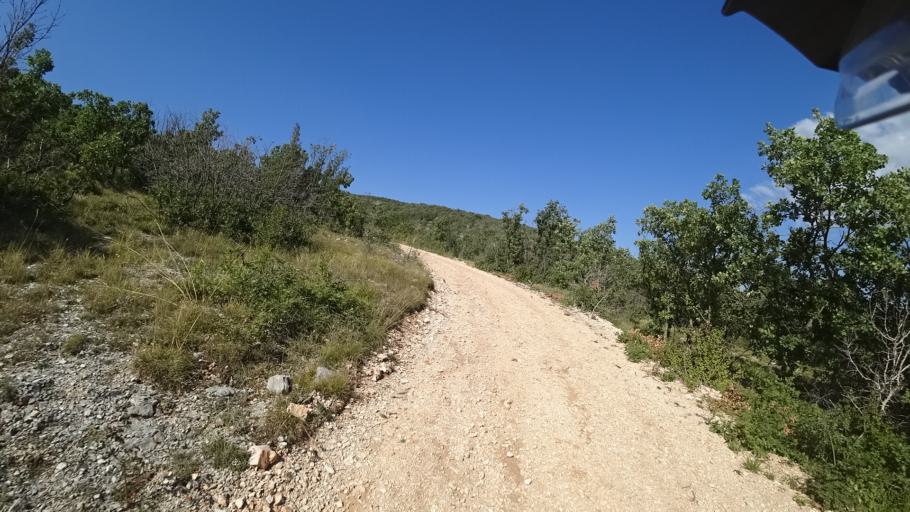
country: HR
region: Sibensko-Kniniska
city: Knin
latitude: 43.9605
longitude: 16.1640
